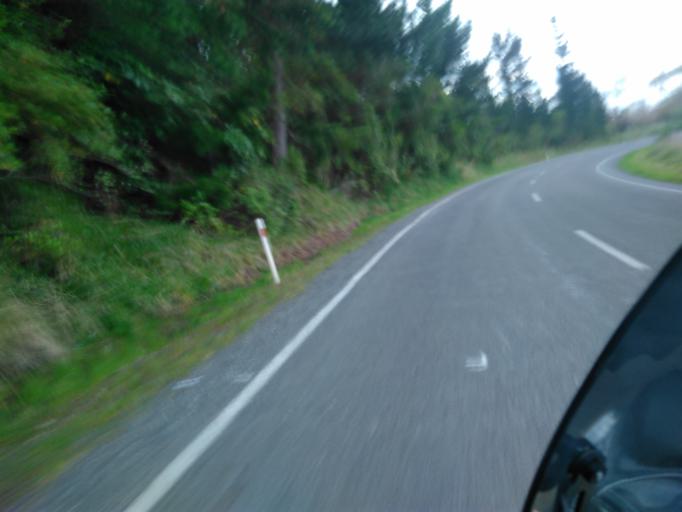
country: NZ
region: Gisborne
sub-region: Gisborne District
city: Gisborne
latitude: -38.6765
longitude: 177.8033
